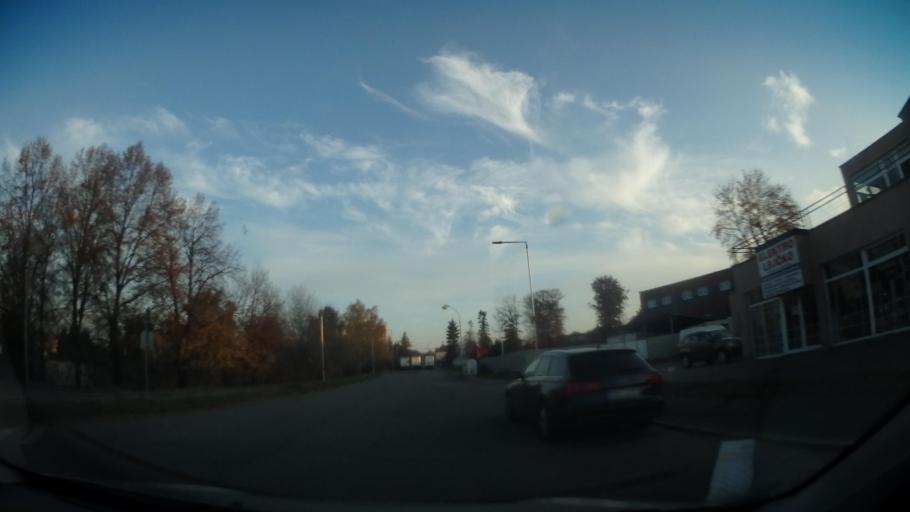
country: CZ
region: Central Bohemia
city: Vlasim
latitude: 49.6992
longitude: 14.9019
